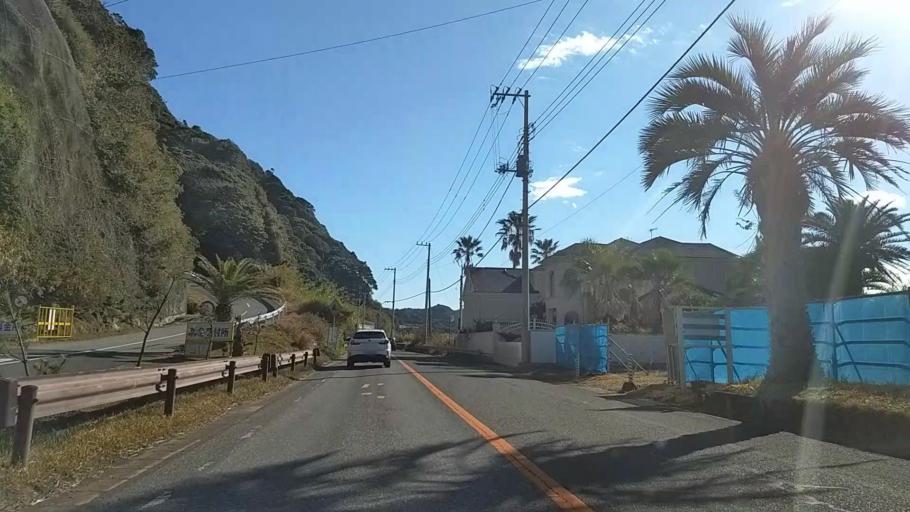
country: JP
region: Chiba
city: Futtsu
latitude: 35.1540
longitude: 139.8216
